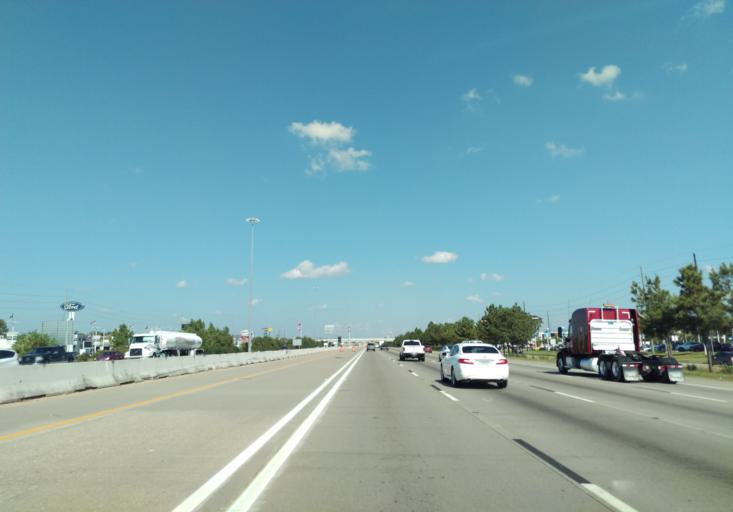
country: US
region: Texas
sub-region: Harris County
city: Spring
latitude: 30.0612
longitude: -95.4333
